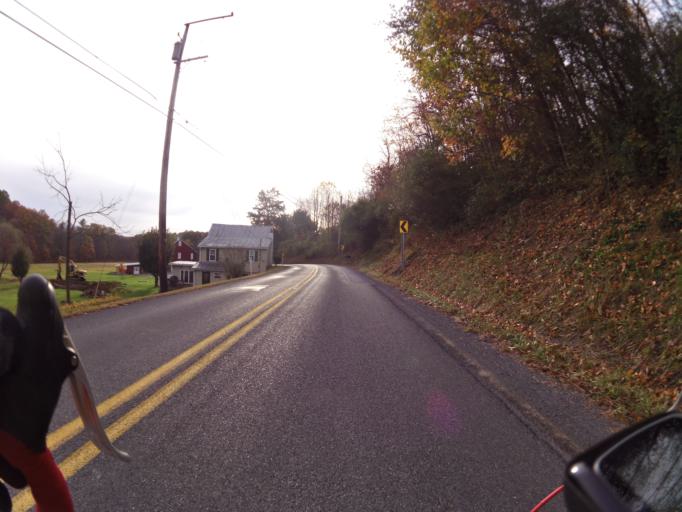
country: US
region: Pennsylvania
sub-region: Union County
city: New Columbia
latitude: 41.0299
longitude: -76.9408
